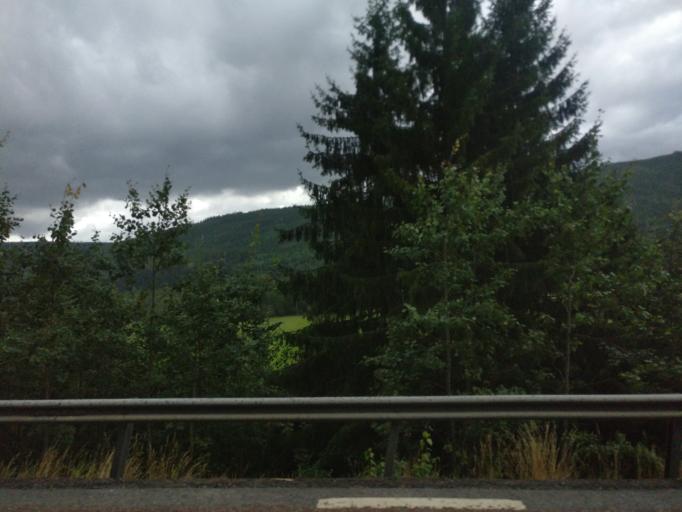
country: SE
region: Vaermland
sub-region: Torsby Kommun
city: Torsby
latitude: 60.7023
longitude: 12.9057
